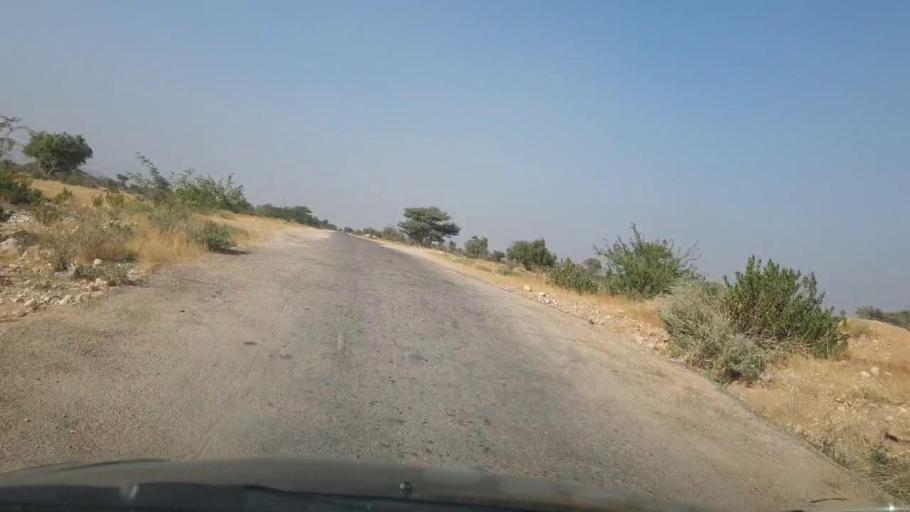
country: PK
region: Sindh
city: Jamshoro
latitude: 25.5607
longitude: 67.8269
